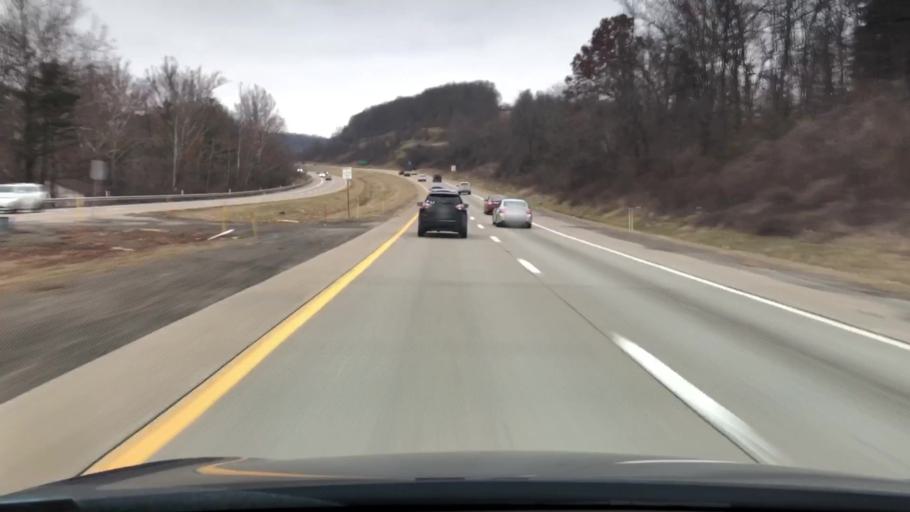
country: US
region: Pennsylvania
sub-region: Greene County
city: Morrisville
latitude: 39.9061
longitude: -80.1497
